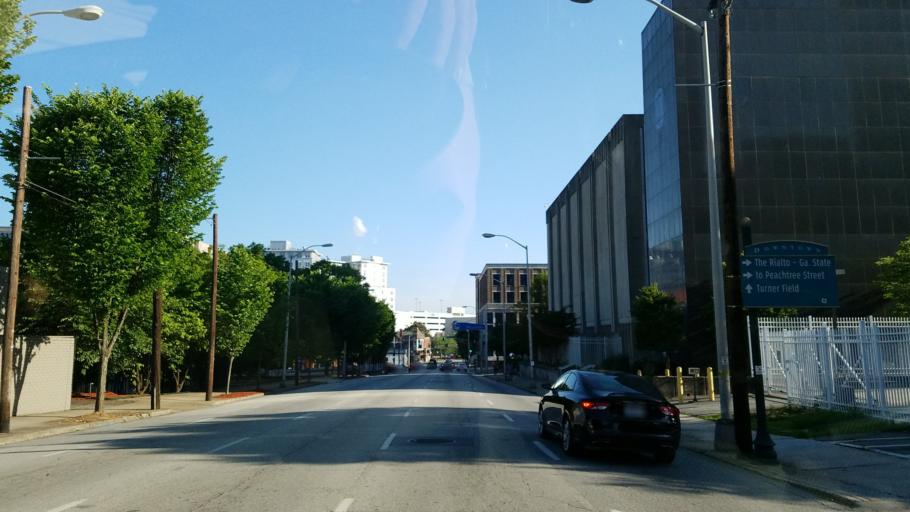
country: US
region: Georgia
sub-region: Fulton County
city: Atlanta
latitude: 33.7570
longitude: -84.3843
